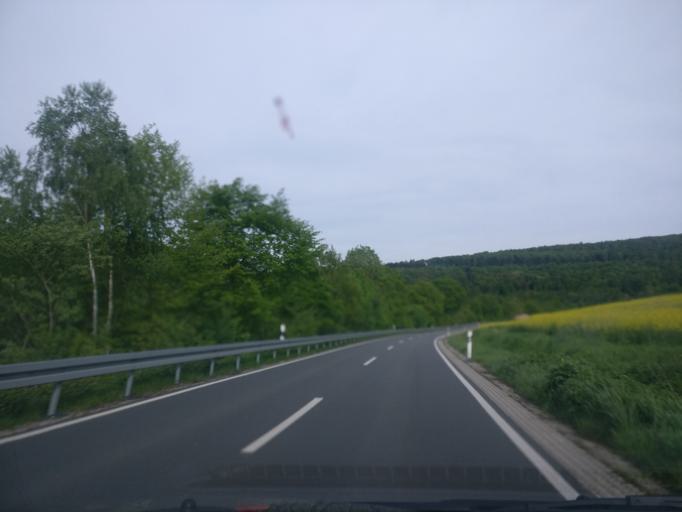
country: DE
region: Hesse
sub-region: Regierungsbezirk Kassel
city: Fuldatal
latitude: 51.3735
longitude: 9.5683
